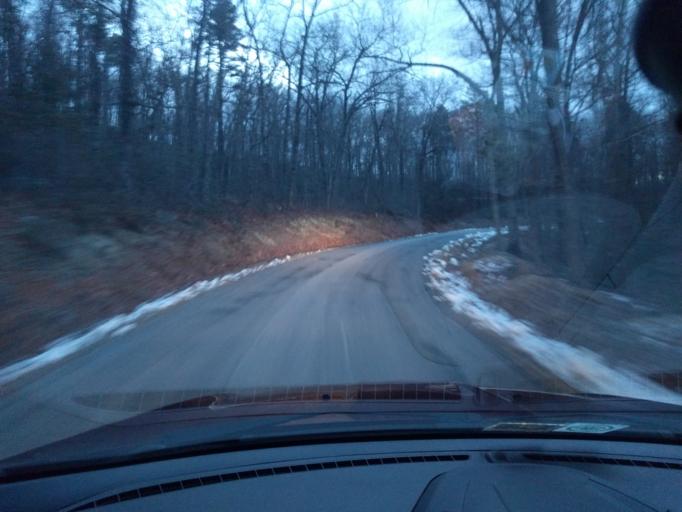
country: US
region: Virginia
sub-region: Alleghany County
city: Clifton Forge
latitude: 37.8604
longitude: -79.8775
